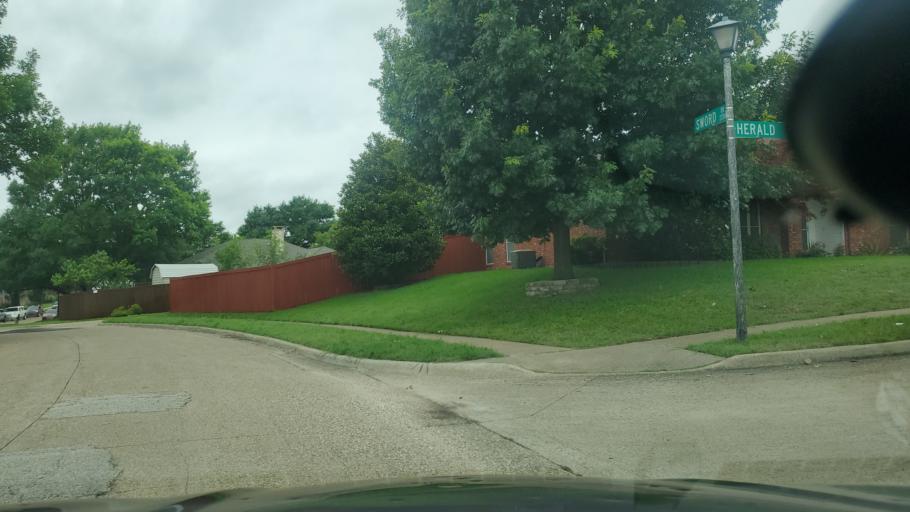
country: US
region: Texas
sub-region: Dallas County
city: Garland
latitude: 32.9544
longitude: -96.6622
